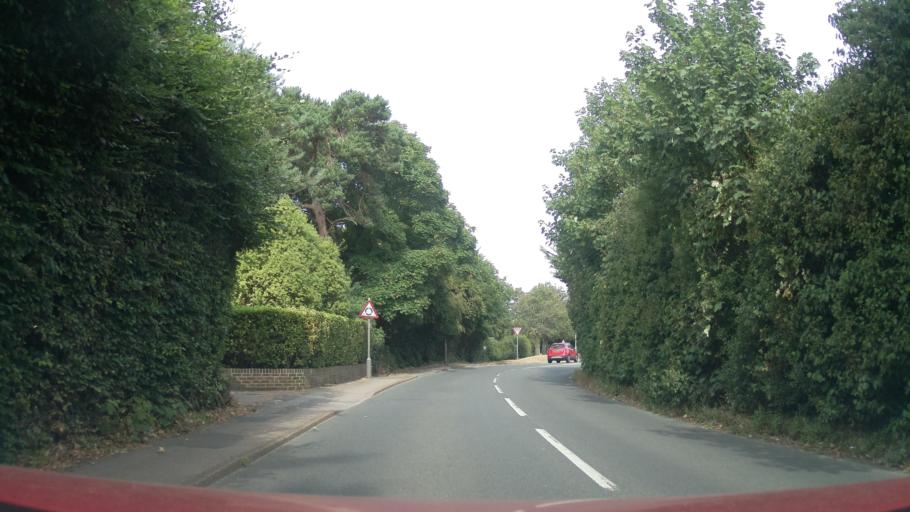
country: GB
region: England
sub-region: Surrey
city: Horley
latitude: 51.1742
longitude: -0.1520
